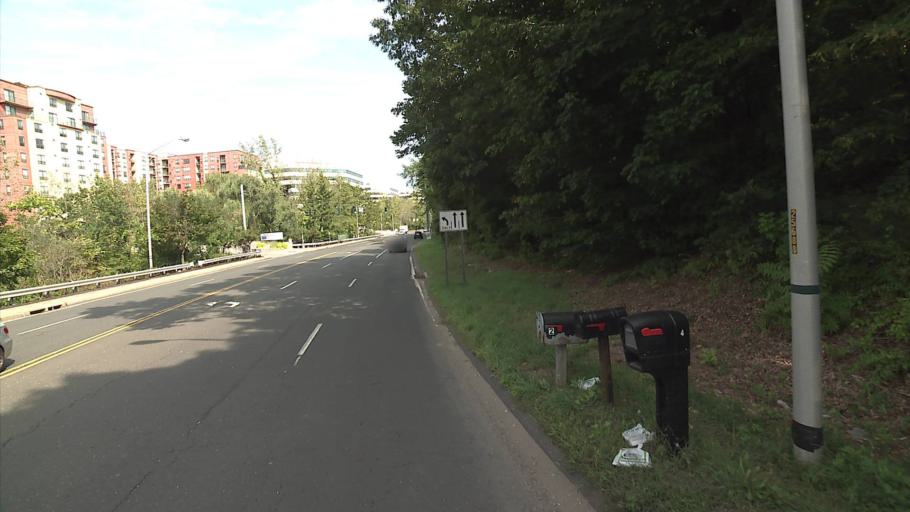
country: US
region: Connecticut
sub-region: Fairfield County
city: Norwalk
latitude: 41.1445
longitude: -73.4262
